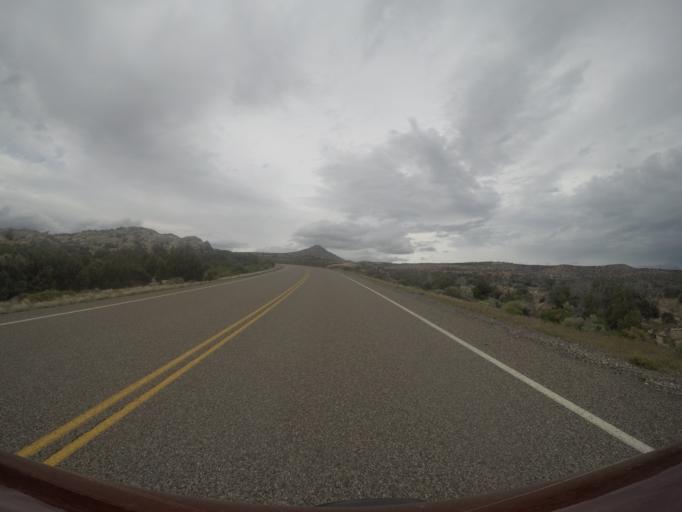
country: US
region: Wyoming
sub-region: Big Horn County
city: Lovell
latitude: 44.9966
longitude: -108.2612
